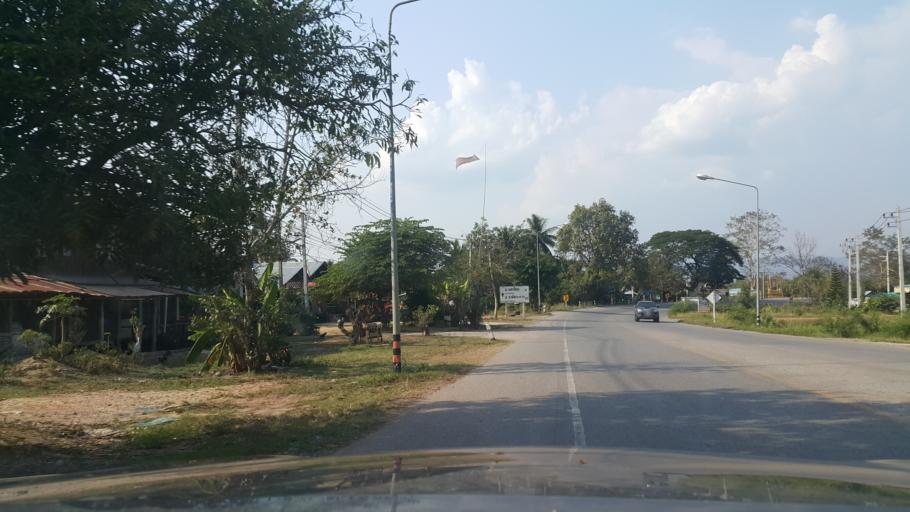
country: TH
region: Phitsanulok
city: Nakhon Thai
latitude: 17.0674
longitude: 100.8094
